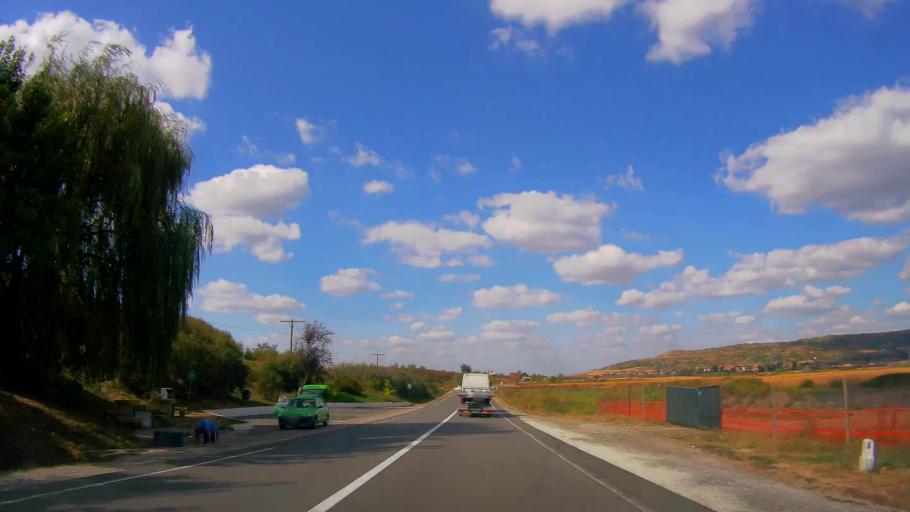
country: RO
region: Salaj
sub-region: Comuna Bobota
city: Dersida
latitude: 47.3719
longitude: 22.7878
